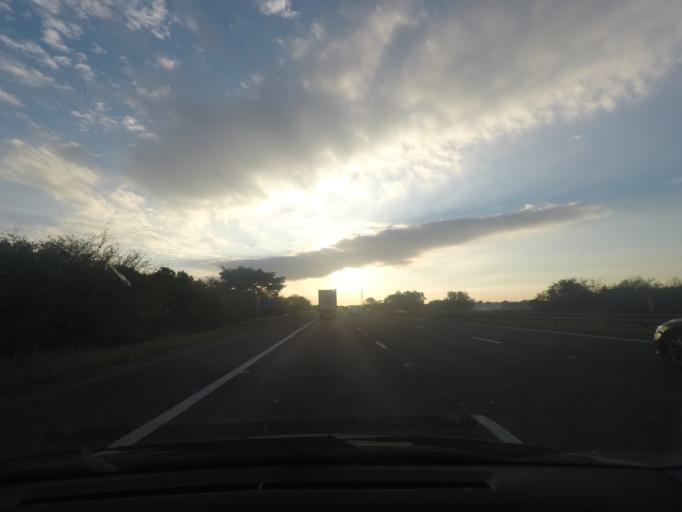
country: GB
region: England
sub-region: North Lincolnshire
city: Brigg
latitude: 53.5583
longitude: -0.5021
